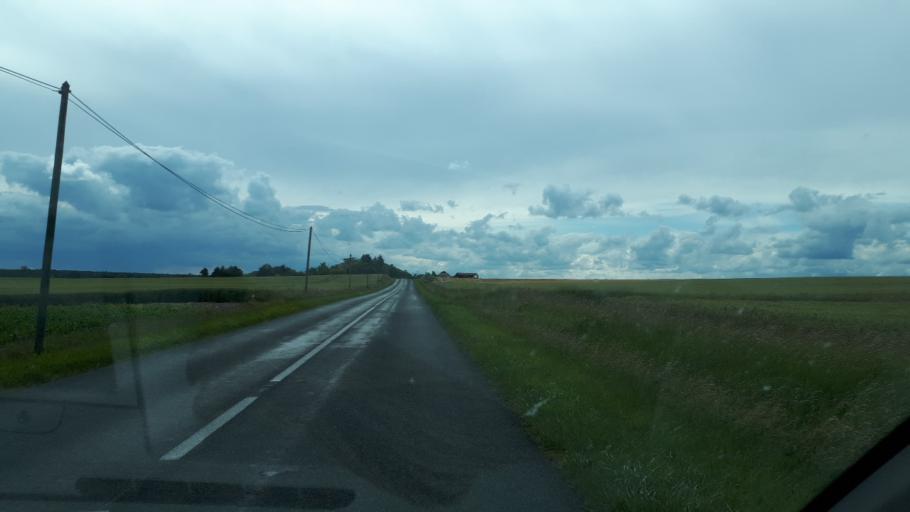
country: FR
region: Centre
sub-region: Departement du Cher
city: Mehun-sur-Yevre
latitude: 47.0815
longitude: 2.2131
